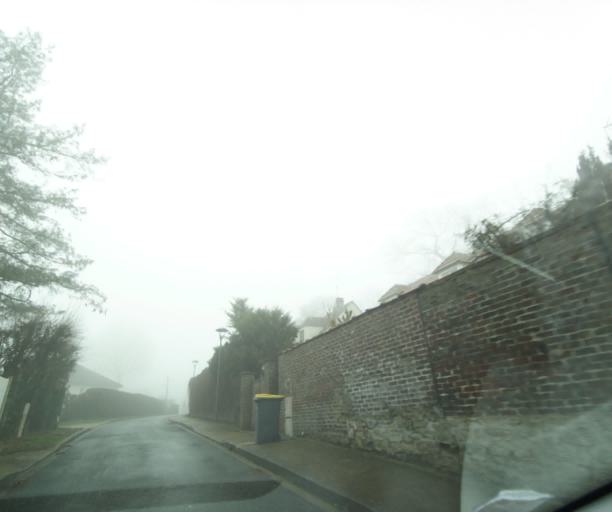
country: FR
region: Ile-de-France
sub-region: Departement de Seine-et-Marne
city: Dammartin-en-Goele
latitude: 49.0546
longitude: 2.6856
